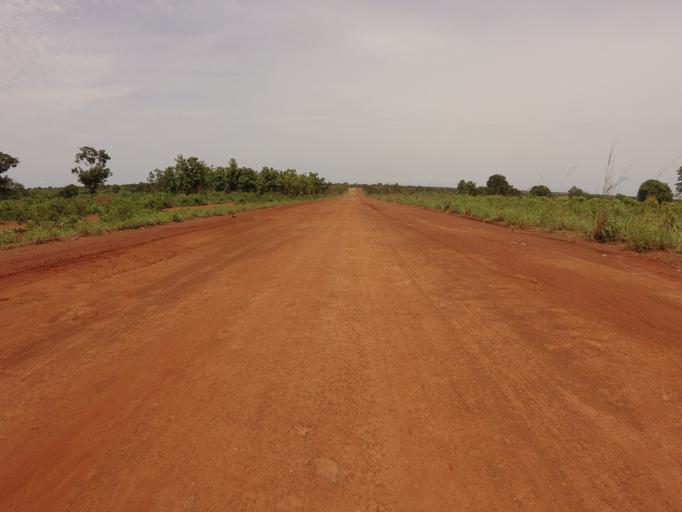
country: GH
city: Kpandae
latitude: 8.7789
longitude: 0.0558
